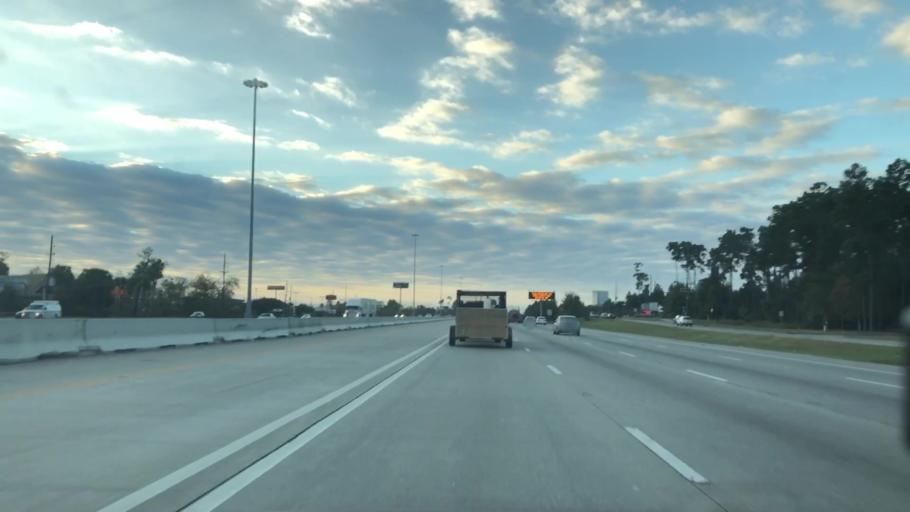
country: US
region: Texas
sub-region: Montgomery County
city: Shenandoah
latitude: 30.1959
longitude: -95.4543
